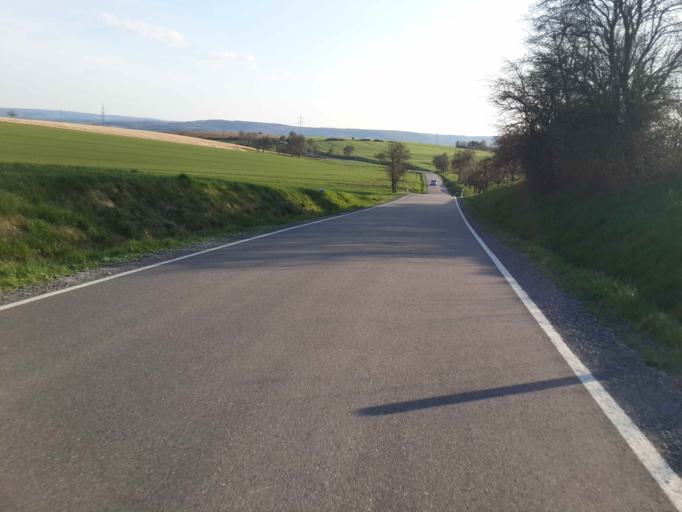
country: DE
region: Baden-Wuerttemberg
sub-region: Regierungsbezirk Stuttgart
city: Widdern
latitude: 49.2654
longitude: 9.4173
